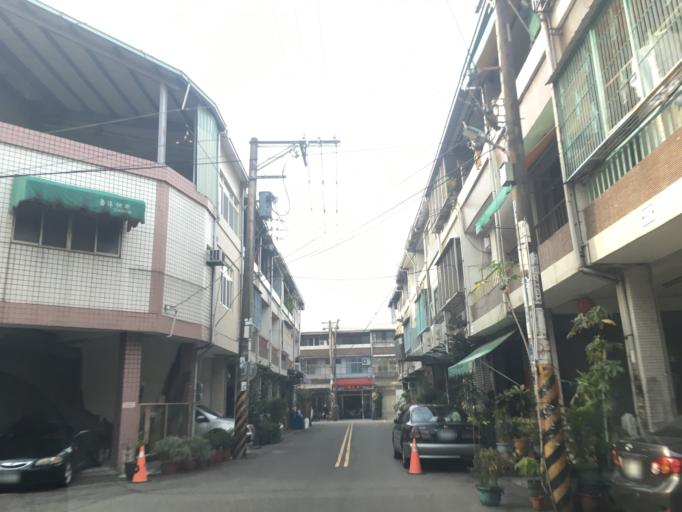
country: TW
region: Taiwan
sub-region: Taichung City
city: Taichung
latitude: 24.1929
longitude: 120.6959
